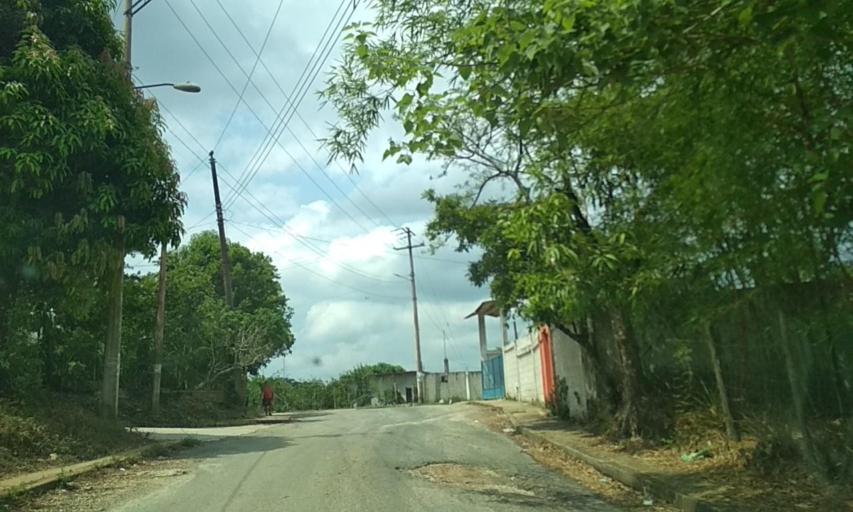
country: MX
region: Veracruz
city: Las Choapas
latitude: 17.8913
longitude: -94.1089
